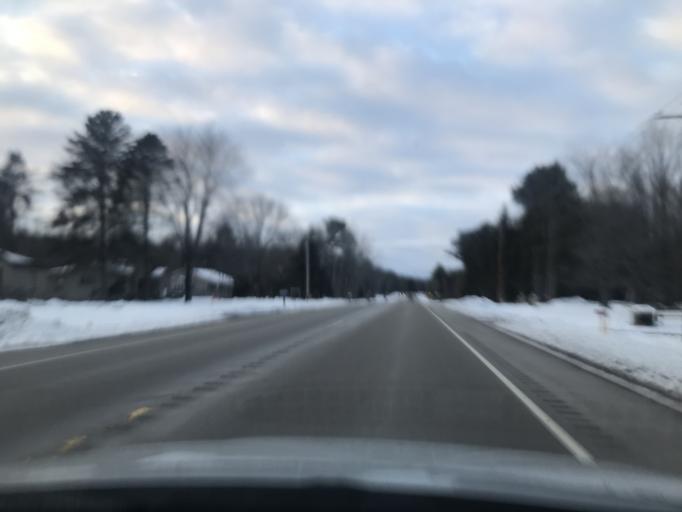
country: US
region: Wisconsin
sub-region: Marinette County
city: Marinette
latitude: 45.1132
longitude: -87.6744
